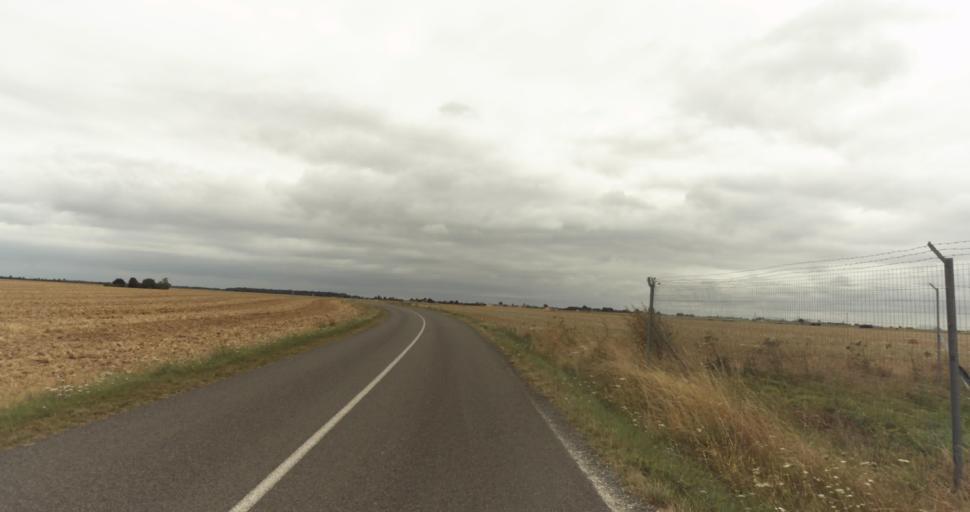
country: FR
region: Haute-Normandie
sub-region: Departement de l'Eure
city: Gravigny
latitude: 49.0445
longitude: 1.2323
